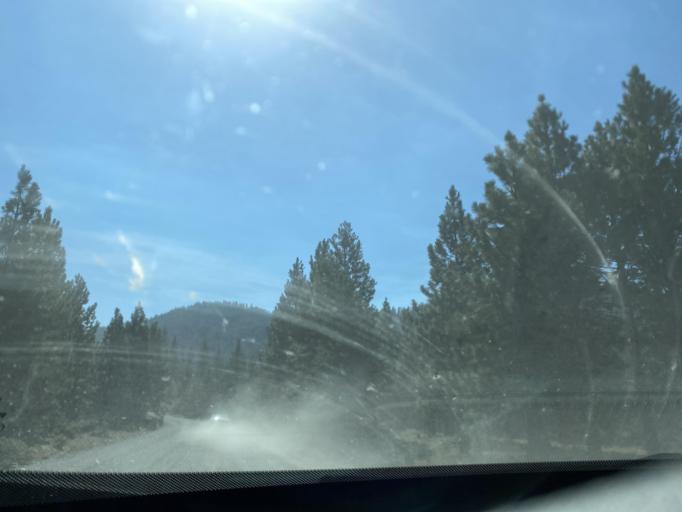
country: US
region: Oregon
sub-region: Deschutes County
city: Deschutes River Woods
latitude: 44.0342
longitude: -121.5258
